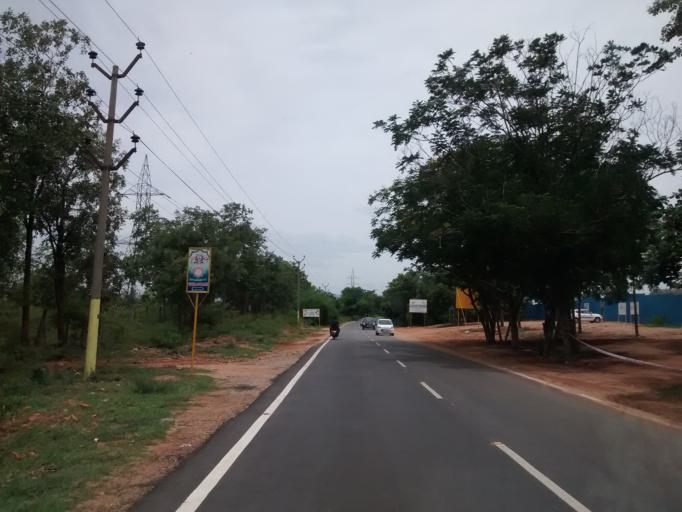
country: IN
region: Andhra Pradesh
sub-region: Chittoor
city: Tirupati
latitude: 13.6287
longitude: 79.3776
